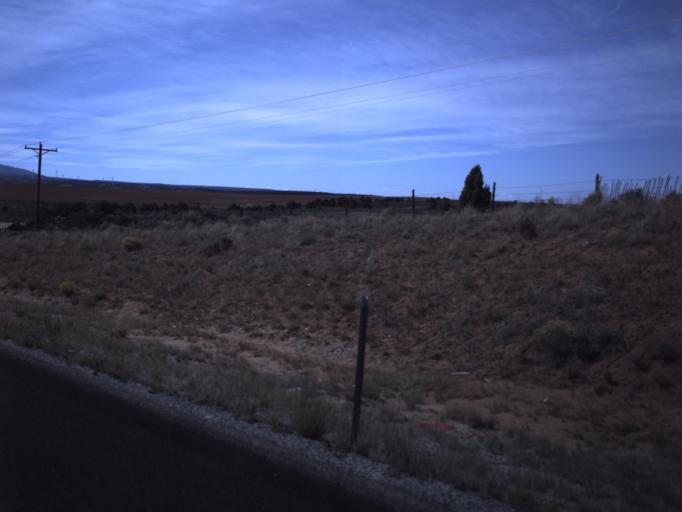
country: US
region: Utah
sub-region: San Juan County
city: Monticello
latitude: 37.8729
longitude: -109.2775
